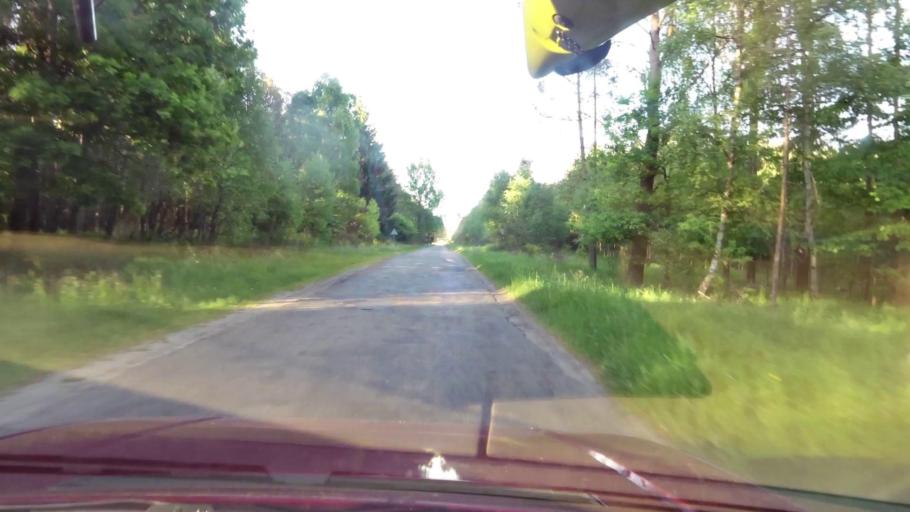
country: PL
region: West Pomeranian Voivodeship
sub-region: Powiat szczecinecki
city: Bialy Bor
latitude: 53.9409
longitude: 16.7623
